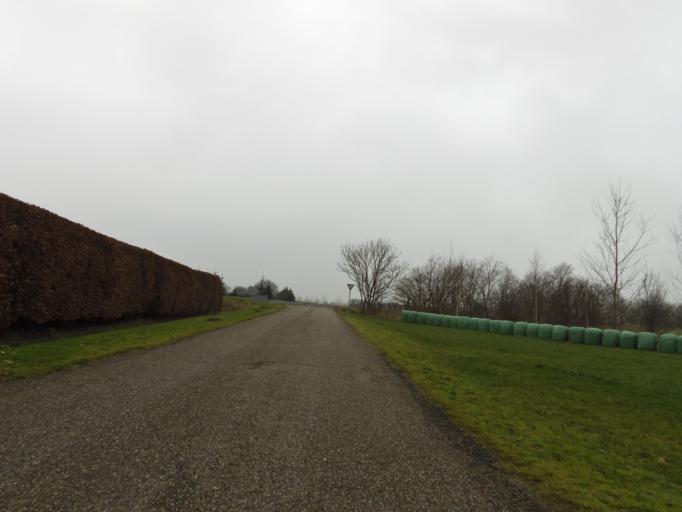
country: DK
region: South Denmark
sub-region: Tonder Kommune
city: Toftlund
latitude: 55.2151
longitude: 9.0488
